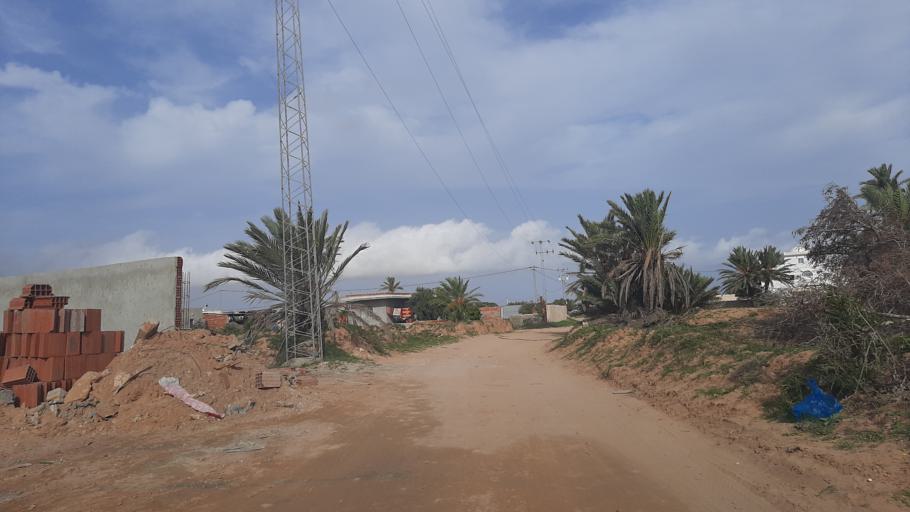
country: TN
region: Madanin
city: Midoun
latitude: 33.8028
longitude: 11.0262
